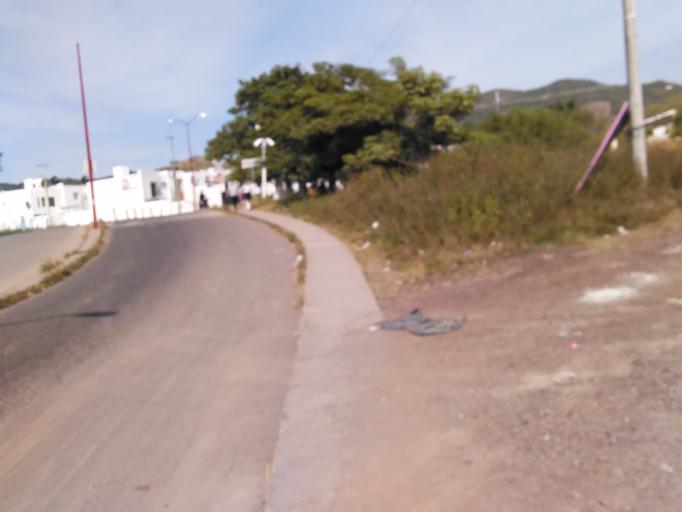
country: MX
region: Nayarit
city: Tepic
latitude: 21.4895
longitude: -104.8557
